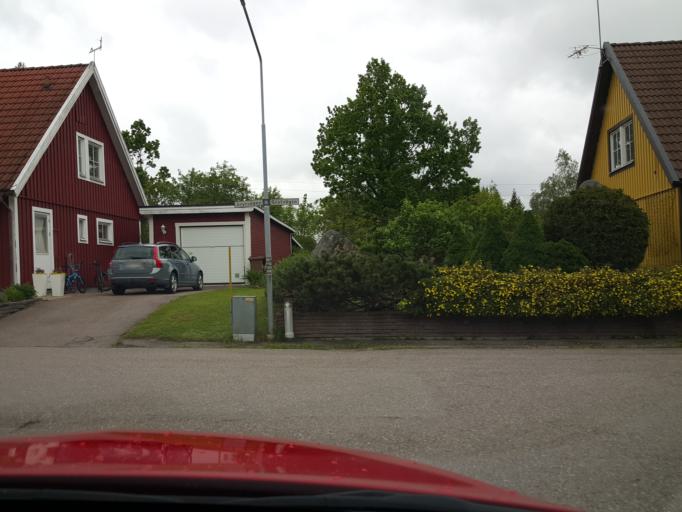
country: SE
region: Uppsala
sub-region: Osthammars Kommun
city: Gimo
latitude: 60.1690
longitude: 18.1720
